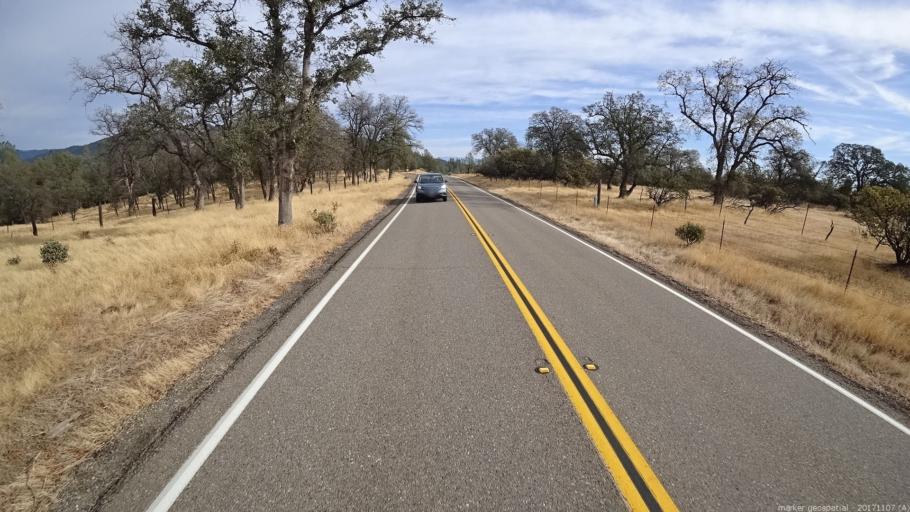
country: US
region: California
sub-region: Shasta County
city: Shasta
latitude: 40.5094
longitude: -122.5360
